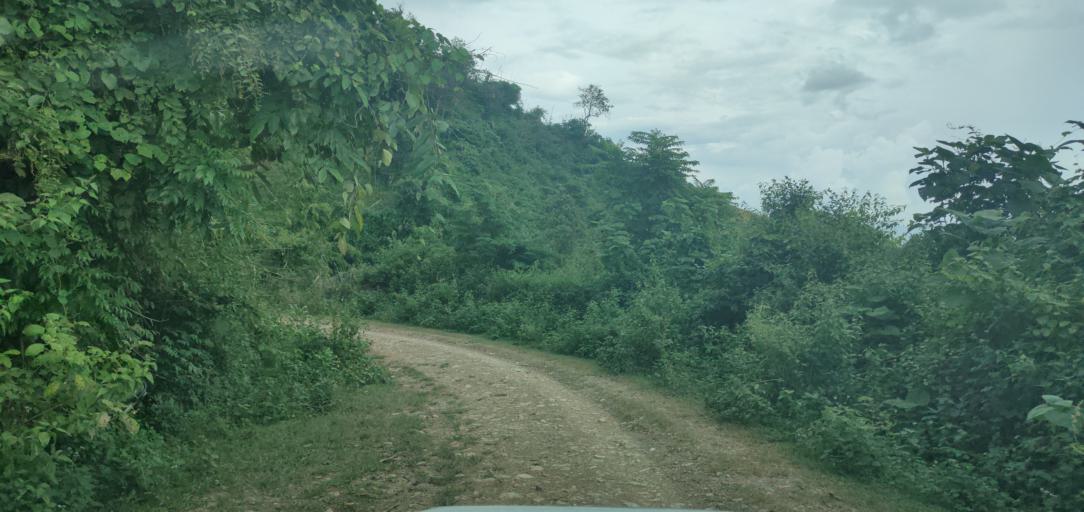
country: LA
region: Phongsali
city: Phongsali
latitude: 21.4439
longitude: 102.3158
